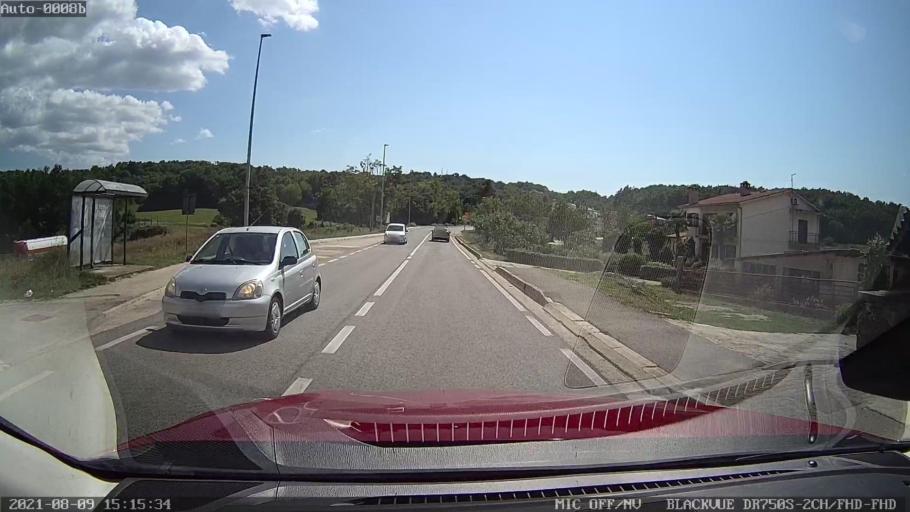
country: HR
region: Istarska
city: Pazin
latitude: 45.2351
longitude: 13.9233
